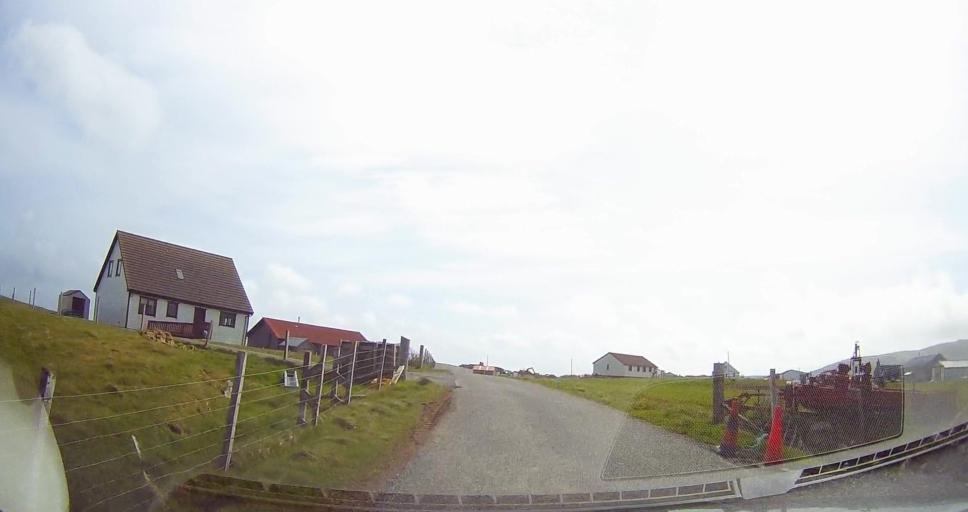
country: GB
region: Scotland
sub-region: Shetland Islands
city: Sandwick
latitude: 60.0406
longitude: -1.2188
